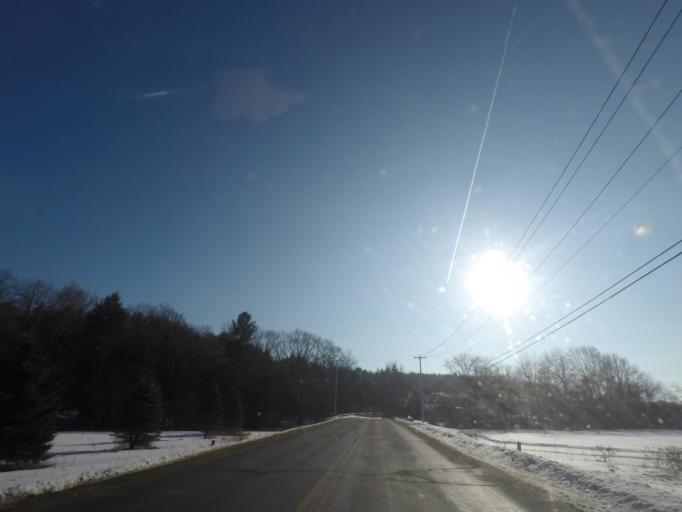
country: US
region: Massachusetts
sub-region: Berkshire County
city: Richmond
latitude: 42.5381
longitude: -73.3968
